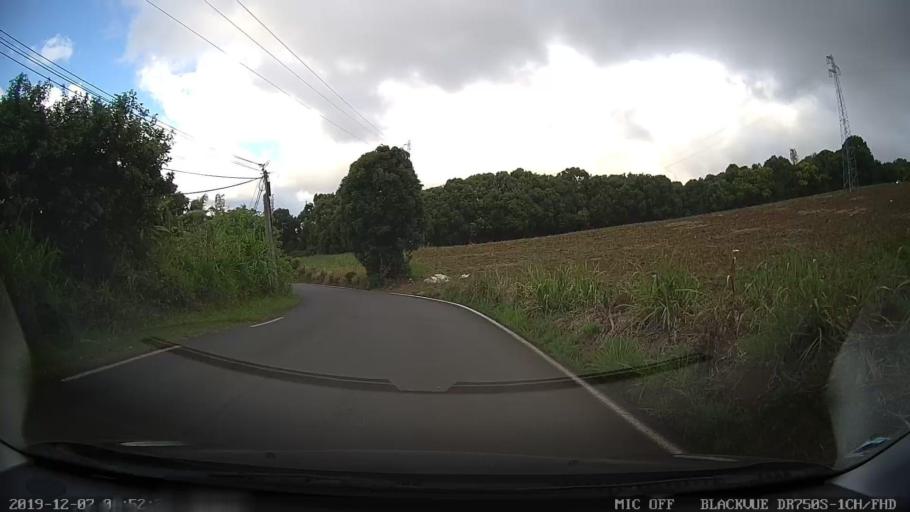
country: RE
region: Reunion
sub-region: Reunion
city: Sainte-Marie
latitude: -20.9395
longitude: 55.5347
